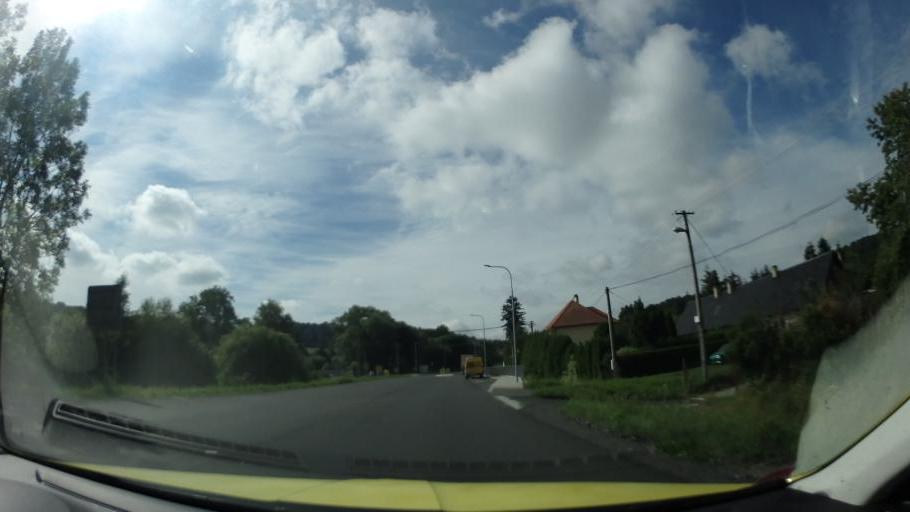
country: CZ
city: Hodslavice
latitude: 49.5659
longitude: 18.0254
